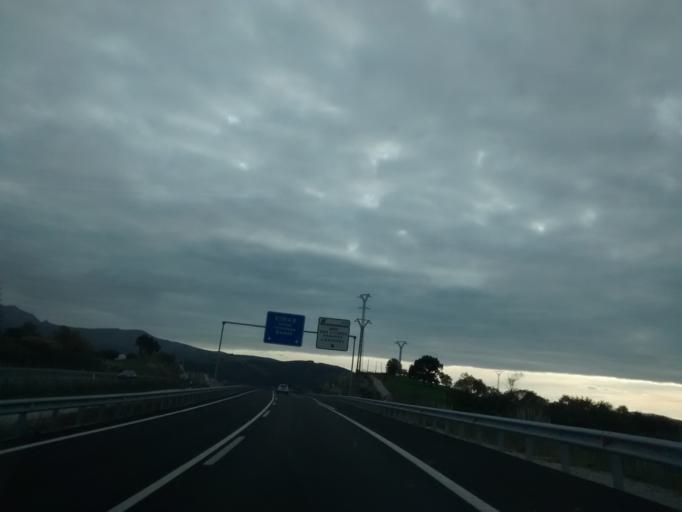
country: ES
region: Cantabria
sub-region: Provincia de Cantabria
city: Lierganes
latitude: 43.3720
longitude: -3.7561
